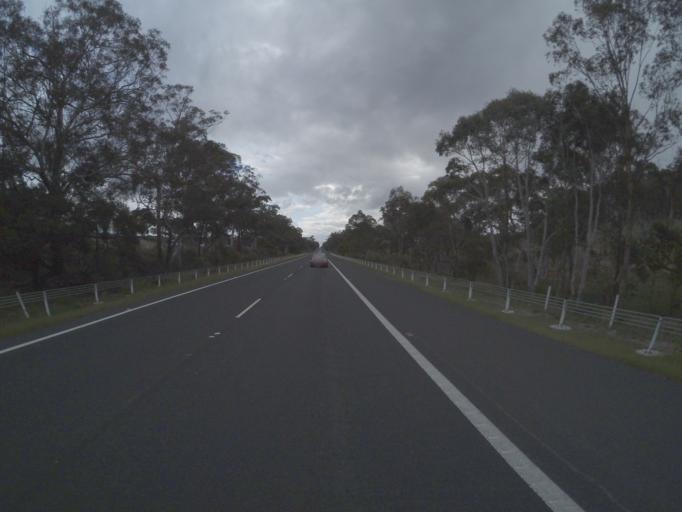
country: AU
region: New South Wales
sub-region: Goulburn Mulwaree
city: Goulburn
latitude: -34.7451
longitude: 149.8739
